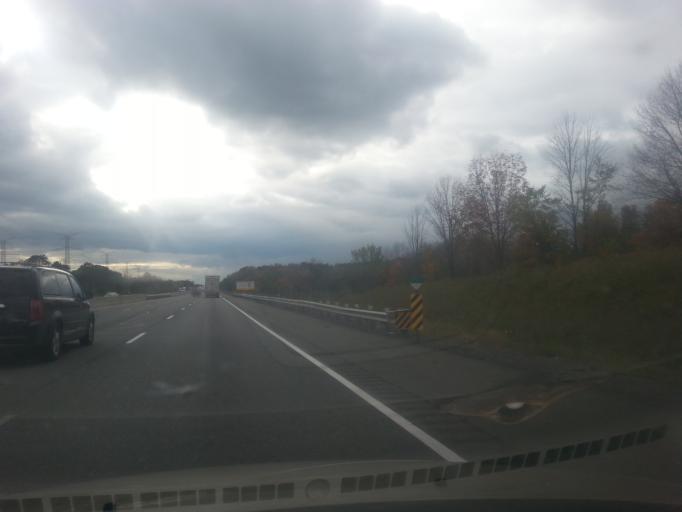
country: CA
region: Ontario
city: Cobourg
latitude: 43.9368
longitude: -78.4637
